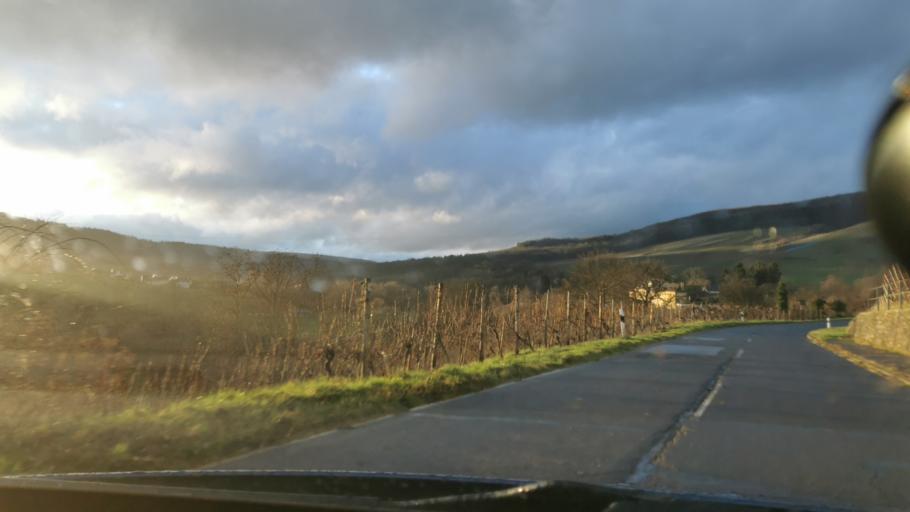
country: DE
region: Rheinland-Pfalz
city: Maring-Noviand
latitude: 49.9324
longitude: 6.9980
